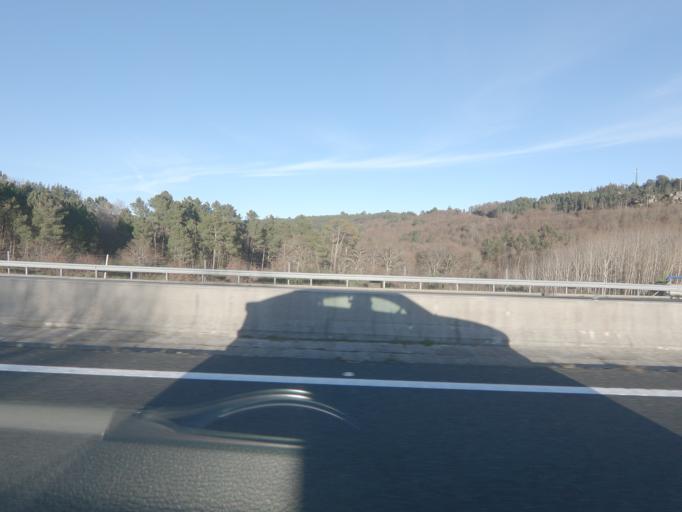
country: ES
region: Galicia
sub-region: Provincia de Ourense
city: Pinor
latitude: 42.4959
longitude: -8.0277
